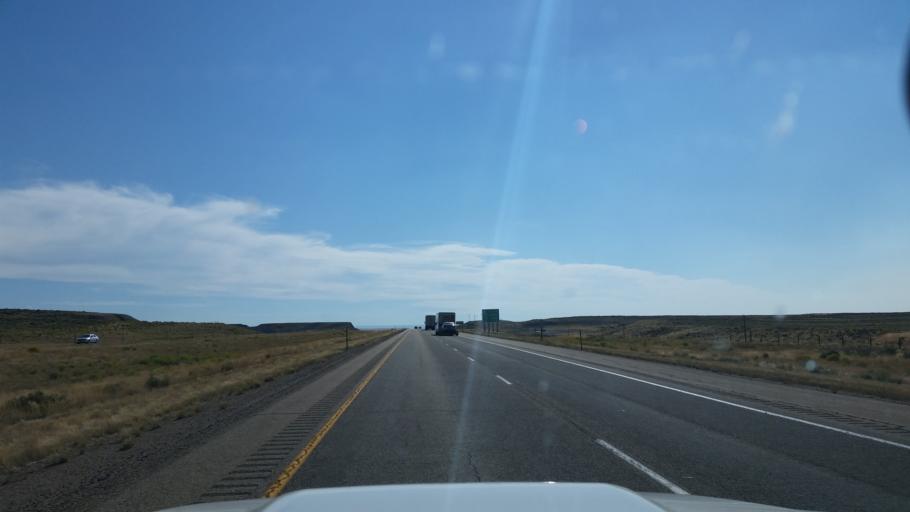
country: US
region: Wyoming
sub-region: Uinta County
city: Lyman
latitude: 41.4069
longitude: -110.1567
